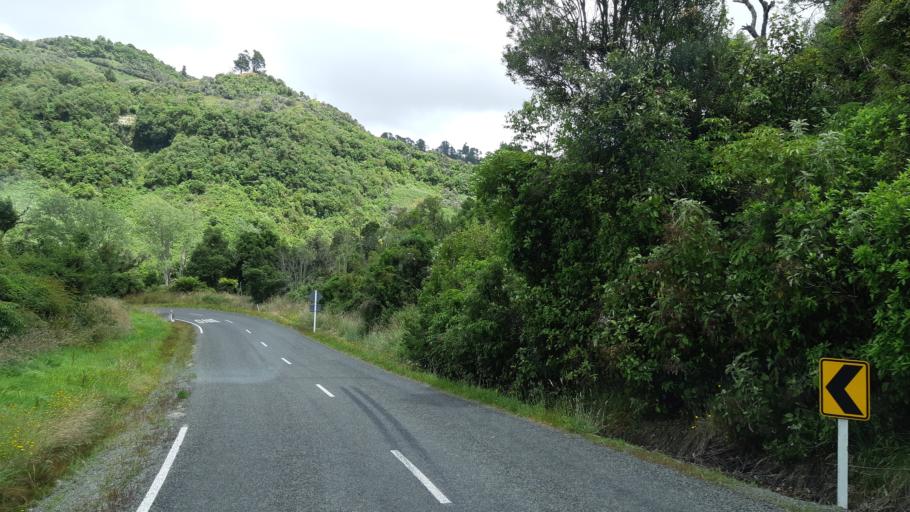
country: NZ
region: Manawatu-Wanganui
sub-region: Palmerston North City
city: Palmerston North
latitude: -39.9365
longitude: 175.9266
